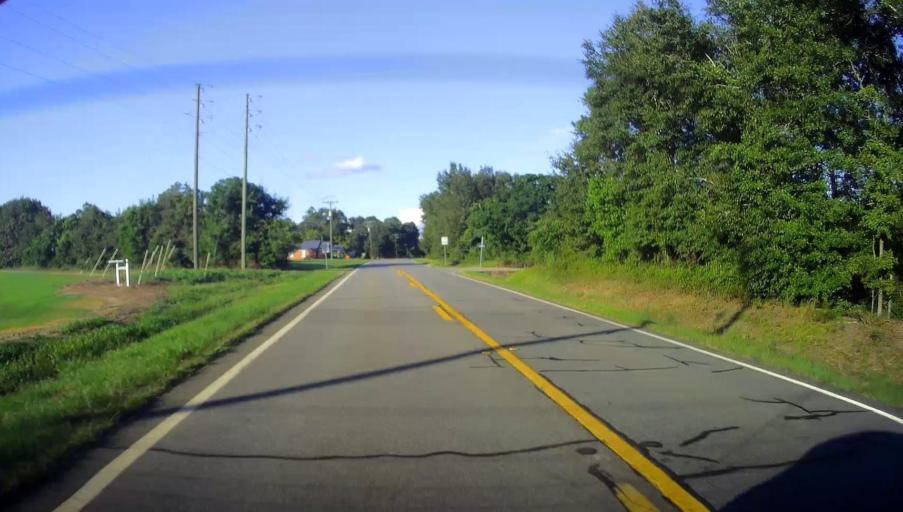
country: US
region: Georgia
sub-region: Pulaski County
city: Hawkinsville
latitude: 32.2741
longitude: -83.5015
